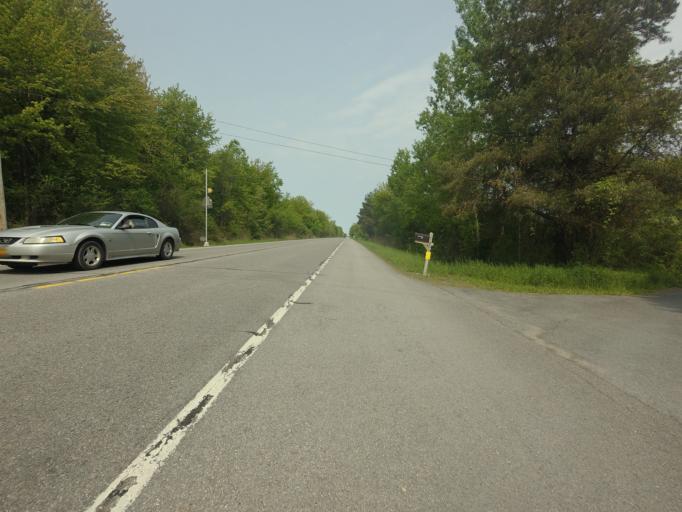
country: US
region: New York
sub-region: Jefferson County
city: Dexter
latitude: 44.0157
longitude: -76.0243
